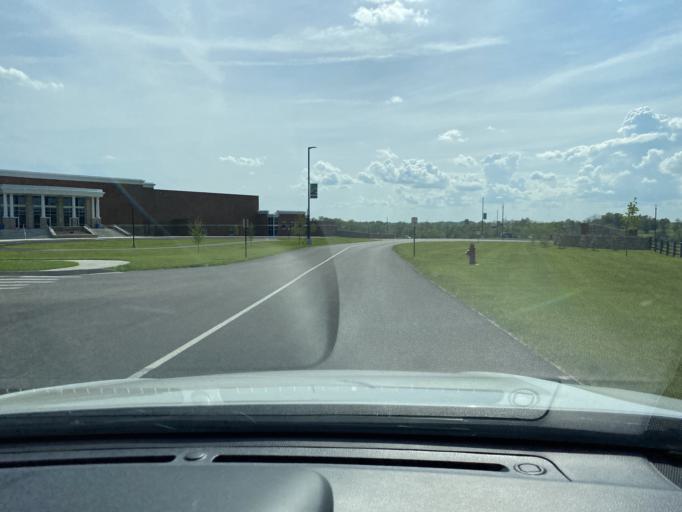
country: US
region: Kentucky
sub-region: Scott County
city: Georgetown
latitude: 38.2169
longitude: -84.5980
